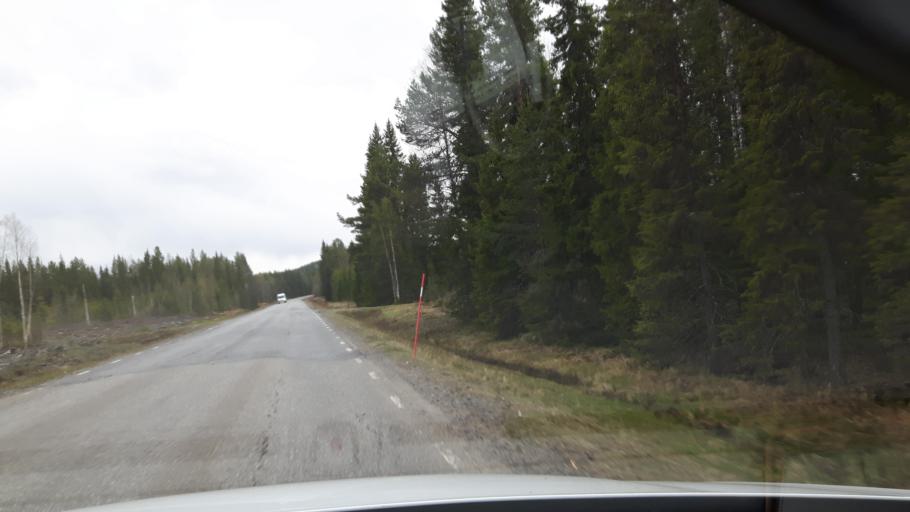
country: SE
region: Vaesterbotten
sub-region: Skelleftea Kommun
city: Burtraesk
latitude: 64.3013
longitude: 20.5275
